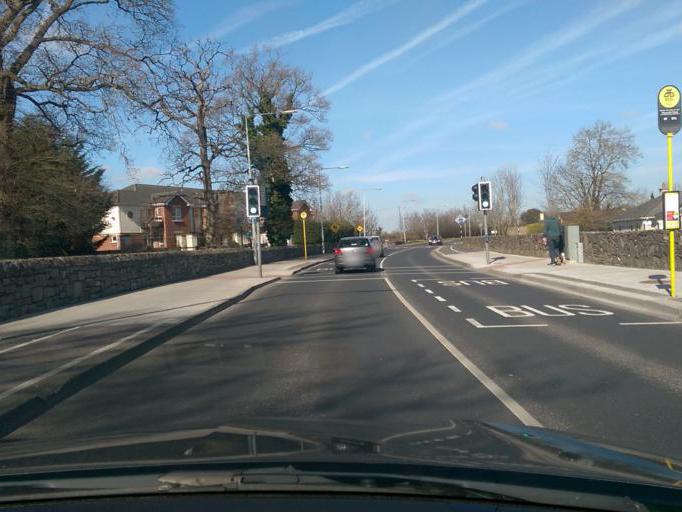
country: IE
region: Leinster
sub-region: Kildare
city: Celbridge
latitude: 53.3520
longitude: -6.5465
